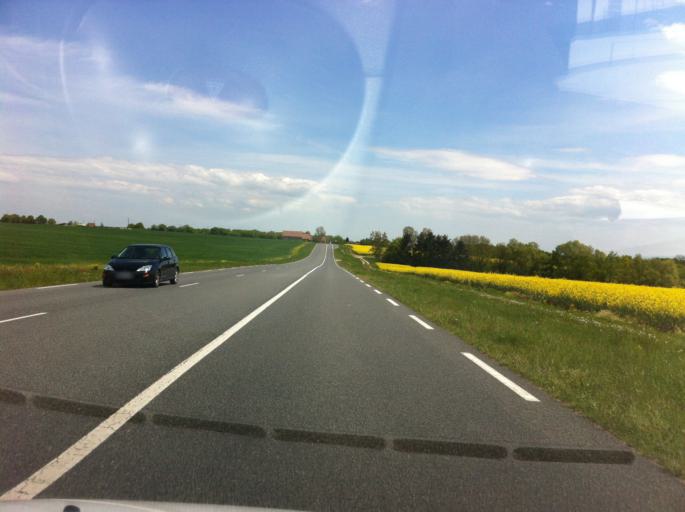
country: FR
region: Auvergne
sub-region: Departement de l'Allier
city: Chantelle
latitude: 46.3171
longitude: 3.1657
